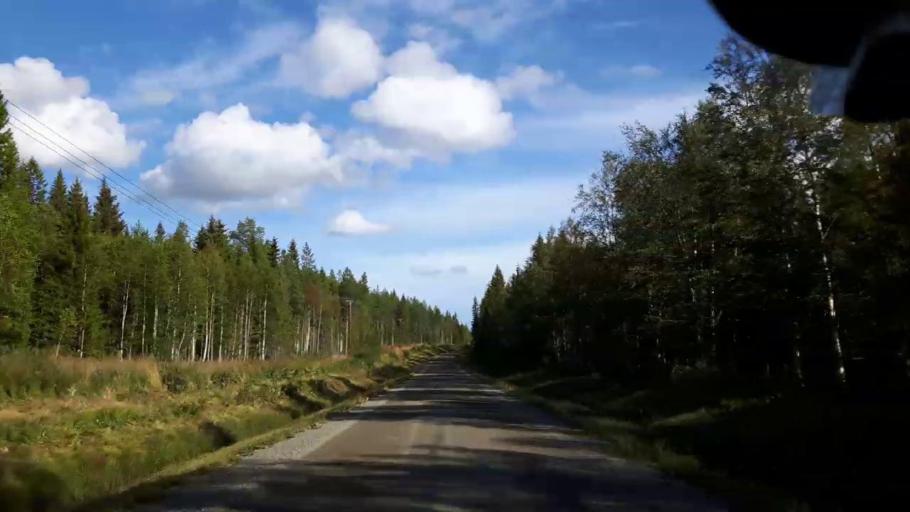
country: SE
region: Jaemtland
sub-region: Ragunda Kommun
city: Hammarstrand
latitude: 63.4349
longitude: 16.0280
